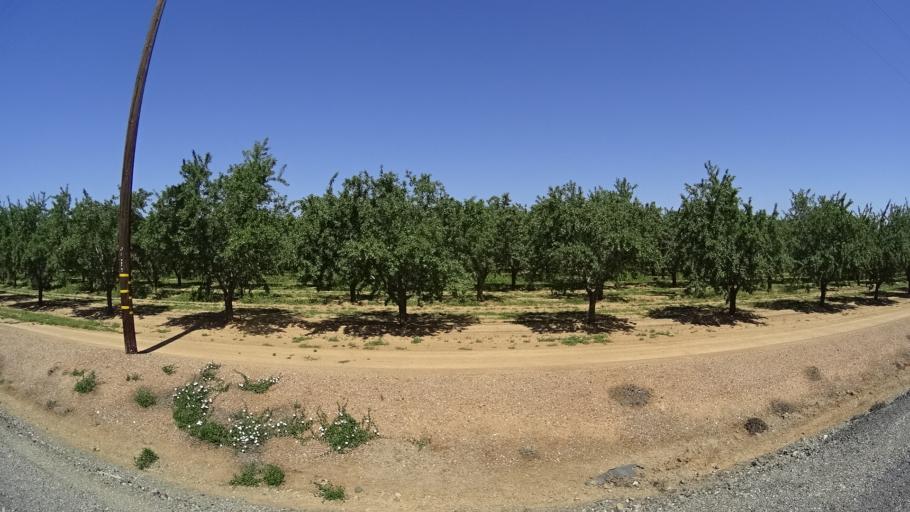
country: US
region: California
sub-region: Glenn County
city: Hamilton City
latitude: 39.7666
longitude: -122.0881
